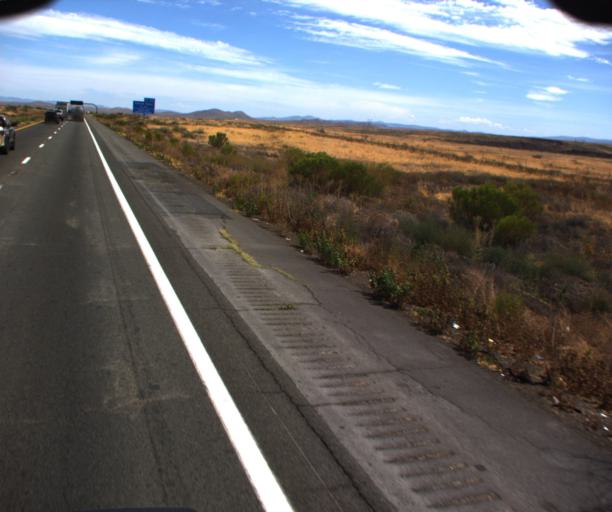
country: US
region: Arizona
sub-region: Yavapai County
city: Black Canyon City
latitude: 34.1808
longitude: -112.1341
